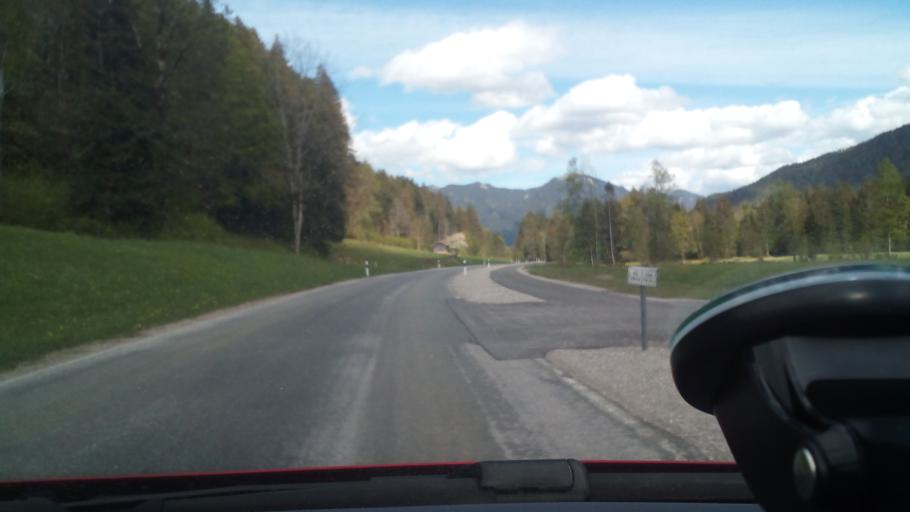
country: DE
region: Bavaria
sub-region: Upper Bavaria
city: Lenggries
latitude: 47.6310
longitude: 11.5417
